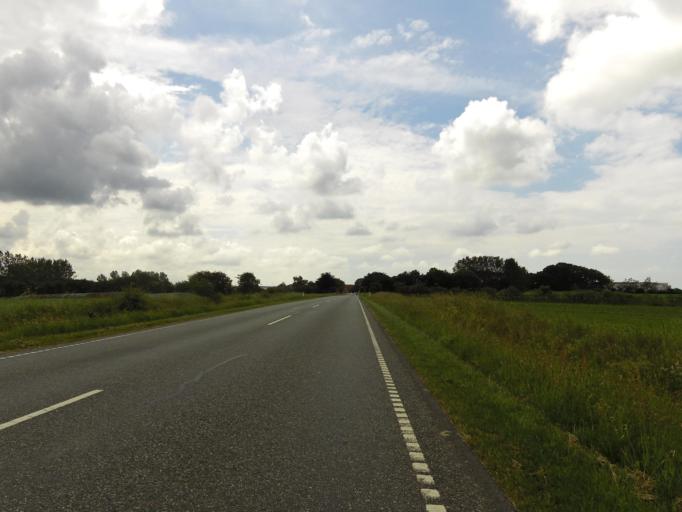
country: DK
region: South Denmark
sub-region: Tonder Kommune
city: Sherrebek
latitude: 55.2137
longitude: 8.8892
